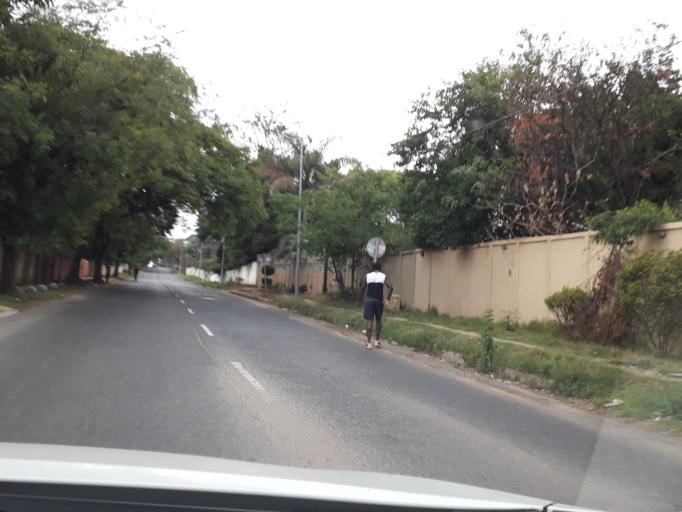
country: ZA
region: Gauteng
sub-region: City of Johannesburg Metropolitan Municipality
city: Johannesburg
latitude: -26.1299
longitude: 28.0897
